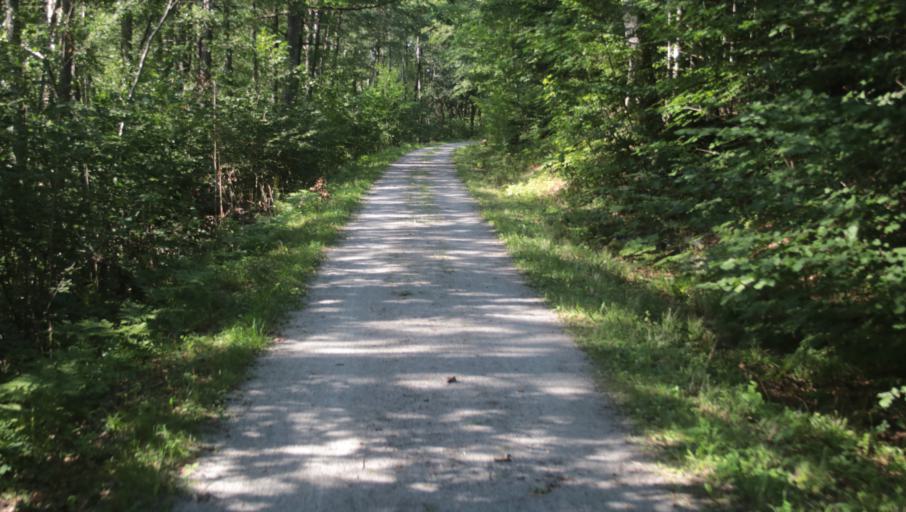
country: SE
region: Blekinge
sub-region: Karlshamns Kommun
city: Svangsta
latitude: 56.3742
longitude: 14.6815
